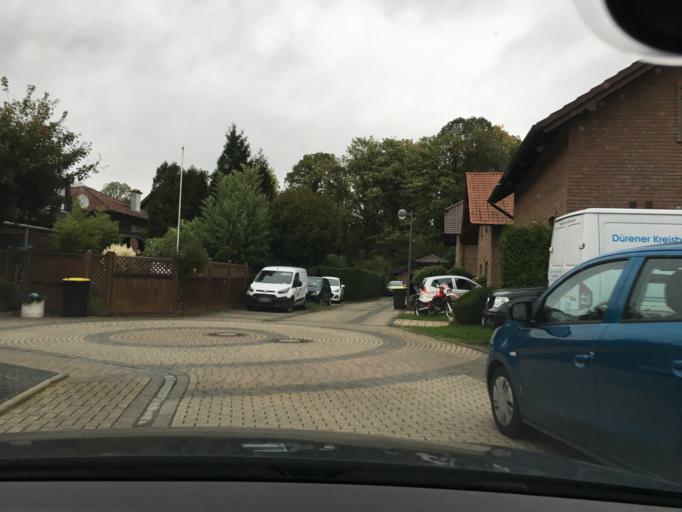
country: DE
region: North Rhine-Westphalia
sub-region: Regierungsbezirk Koln
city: Kreuzau
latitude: 50.7411
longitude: 6.4982
